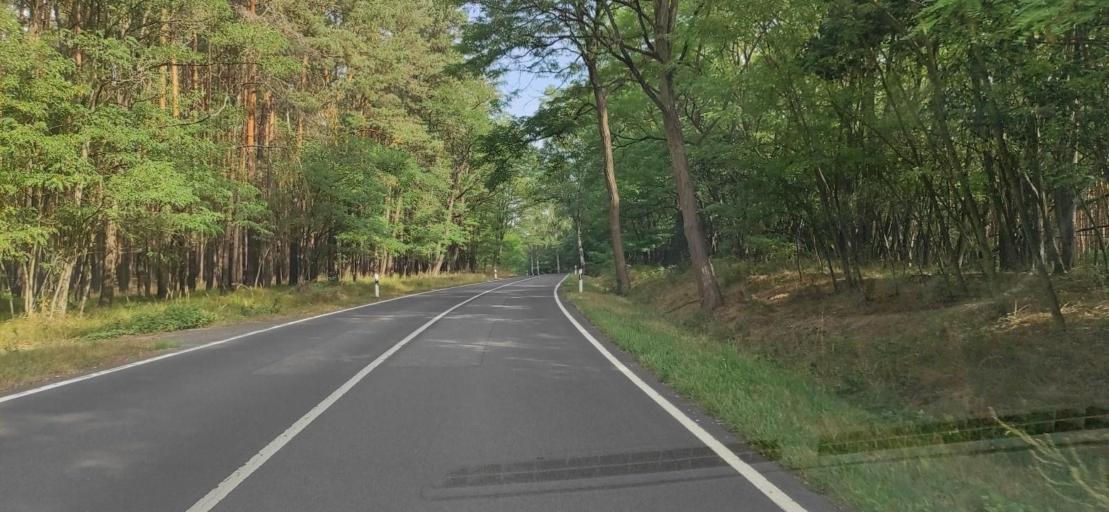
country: DE
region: Brandenburg
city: Forst
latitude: 51.6826
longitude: 14.7220
